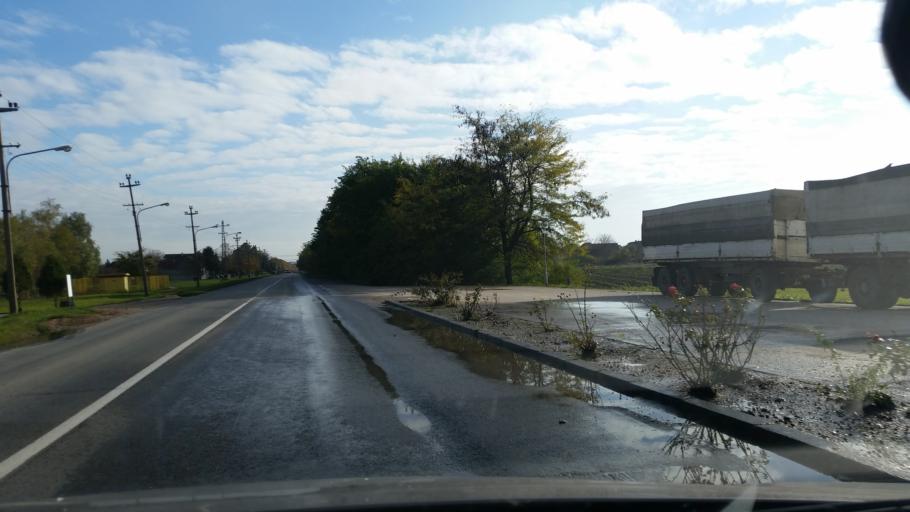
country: RS
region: Autonomna Pokrajina Vojvodina
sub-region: Srednjebanatski Okrug
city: Zrenjanin
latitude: 45.3983
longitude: 20.3776
